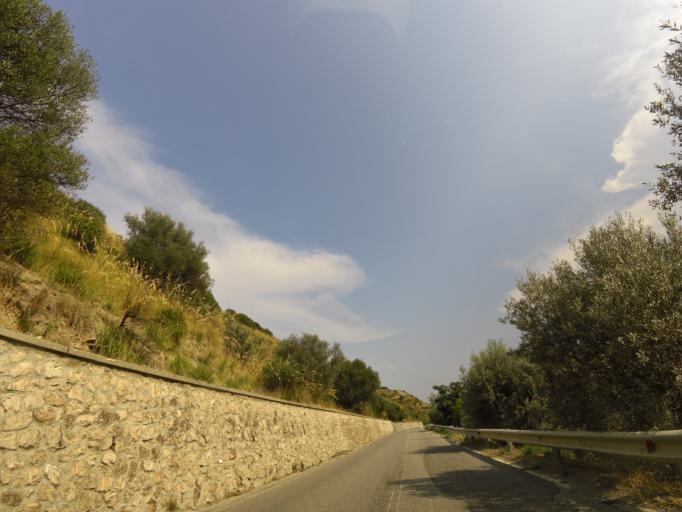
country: IT
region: Calabria
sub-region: Provincia di Reggio Calabria
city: Monasterace
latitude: 38.4601
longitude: 16.5212
